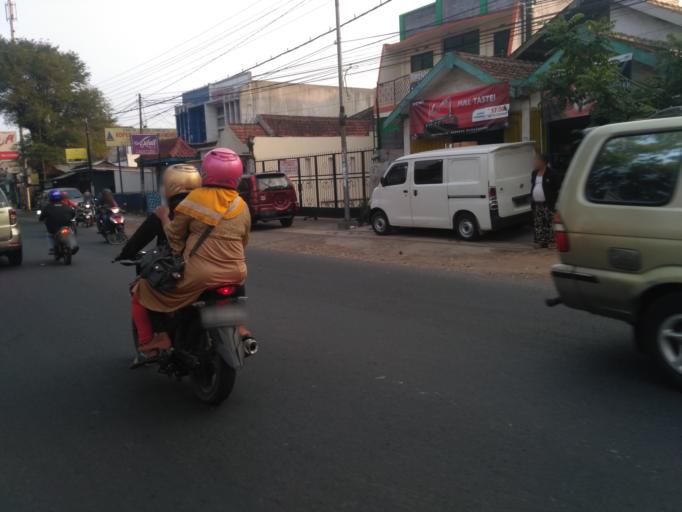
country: ID
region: East Java
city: Kebonsari
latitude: -8.0132
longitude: 112.6205
